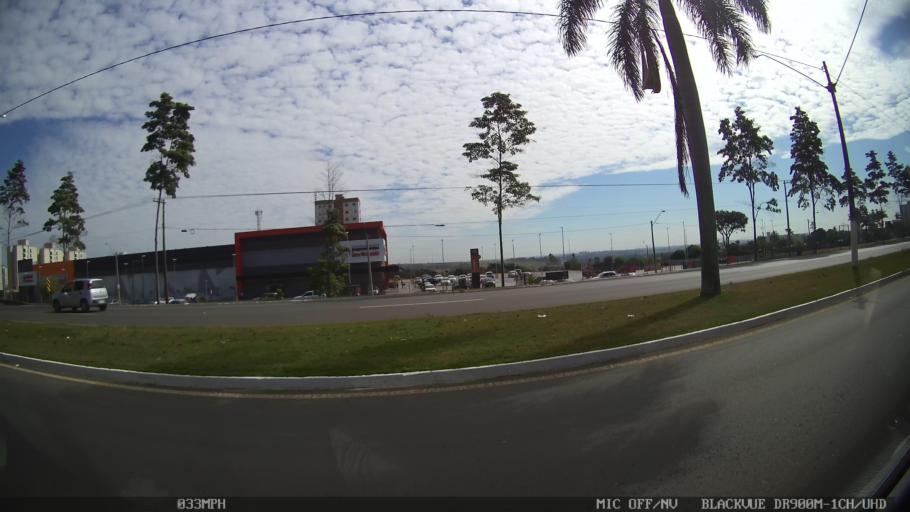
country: BR
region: Sao Paulo
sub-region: Santa Barbara D'Oeste
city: Santa Barbara d'Oeste
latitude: -22.7576
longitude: -47.4315
